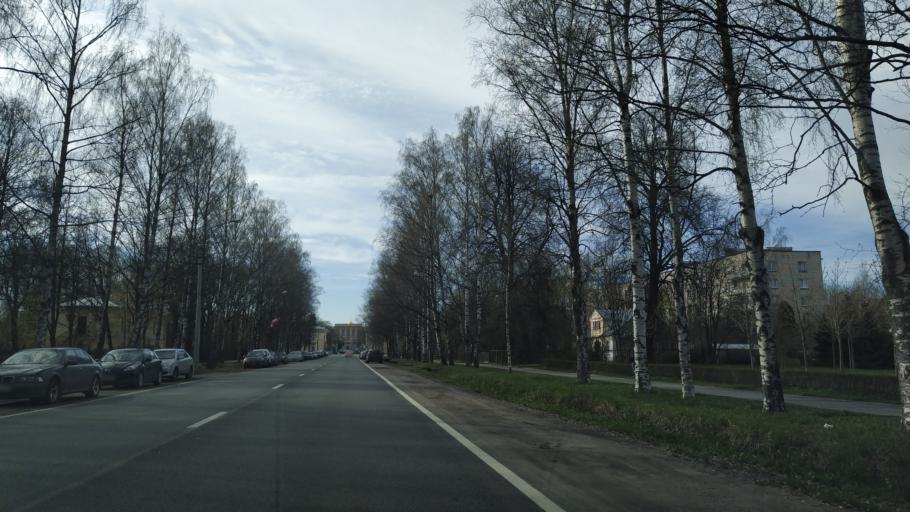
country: RU
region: St.-Petersburg
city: Pushkin
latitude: 59.7146
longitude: 30.4250
